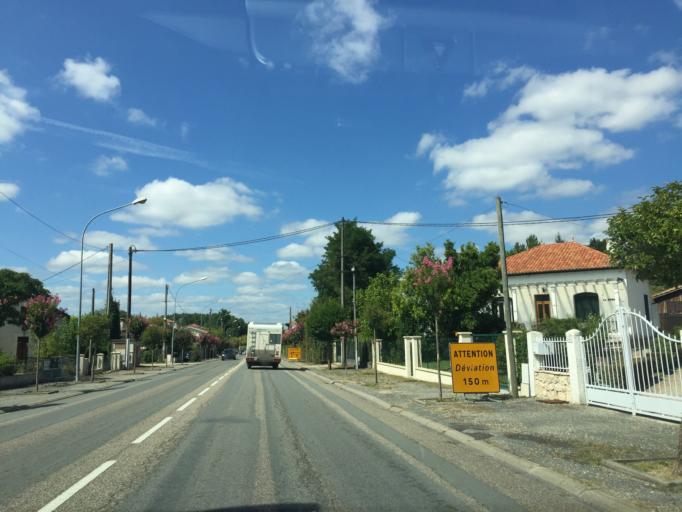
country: FR
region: Aquitaine
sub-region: Departement du Lot-et-Garonne
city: Casteljaloux
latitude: 44.3104
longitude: 0.0930
